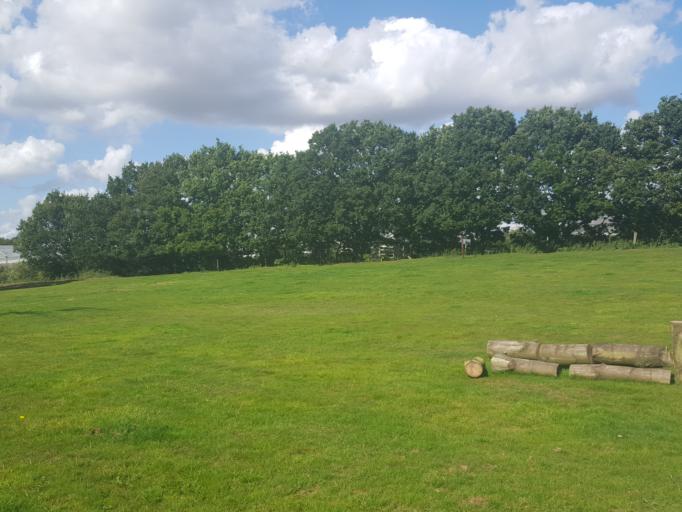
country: GB
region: England
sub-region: Essex
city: Alresford
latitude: 51.8519
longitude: 1.0196
